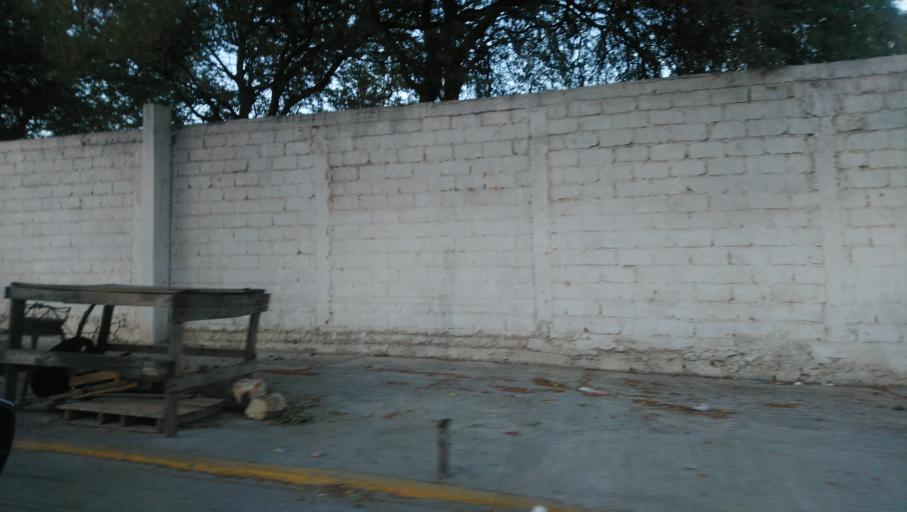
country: MX
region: Oaxaca
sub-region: Salina Cruz
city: Salina Cruz
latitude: 16.1848
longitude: -95.1986
